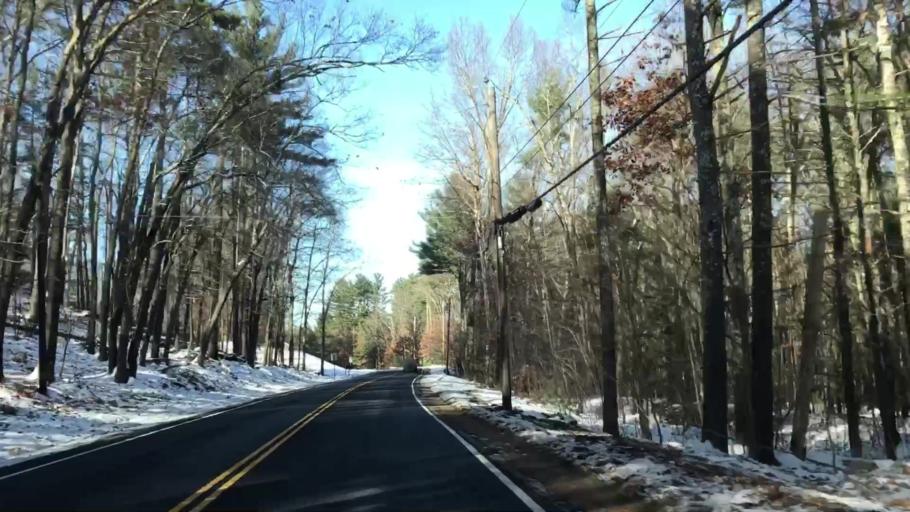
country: US
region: New Hampshire
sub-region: Hillsborough County
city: Milford
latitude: 42.8418
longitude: -71.6134
